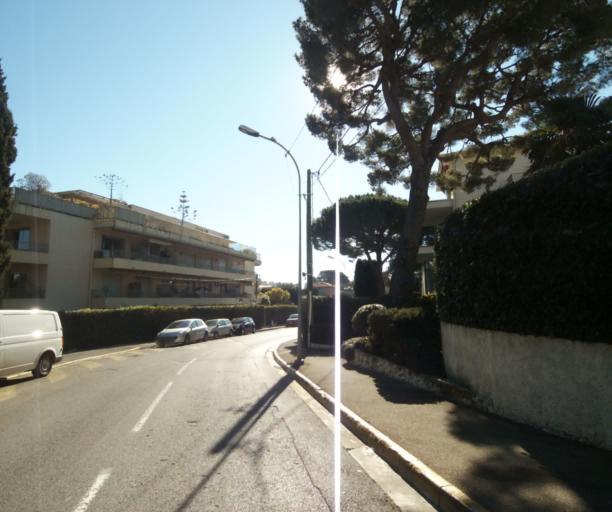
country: FR
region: Provence-Alpes-Cote d'Azur
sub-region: Departement des Alpes-Maritimes
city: Antibes
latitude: 43.5701
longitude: 7.1193
